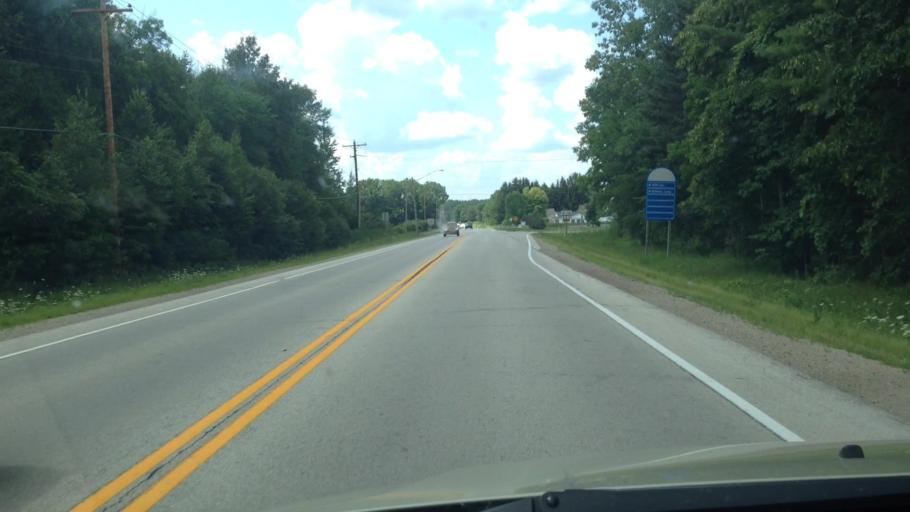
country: US
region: Wisconsin
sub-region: Brown County
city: Suamico
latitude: 44.6438
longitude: -88.0885
